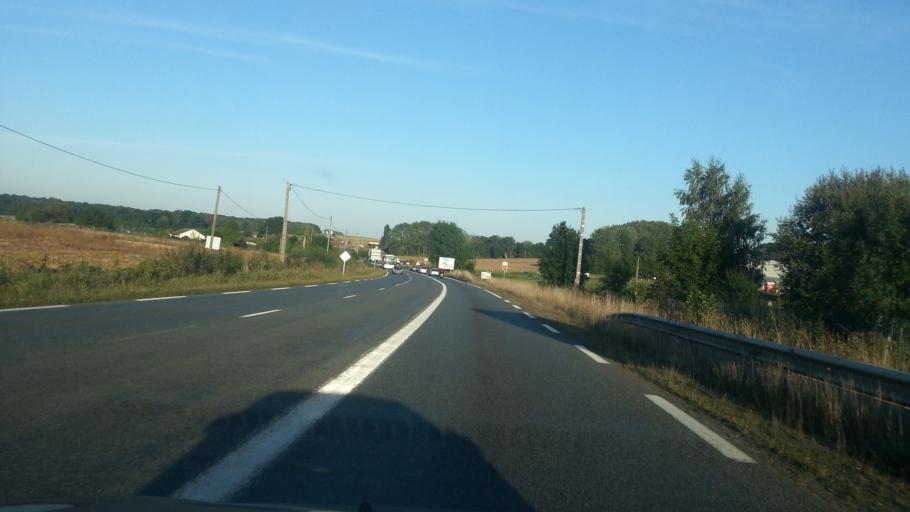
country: FR
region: Picardie
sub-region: Departement de l'Oise
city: Le Meux
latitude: 49.4025
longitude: 2.7404
